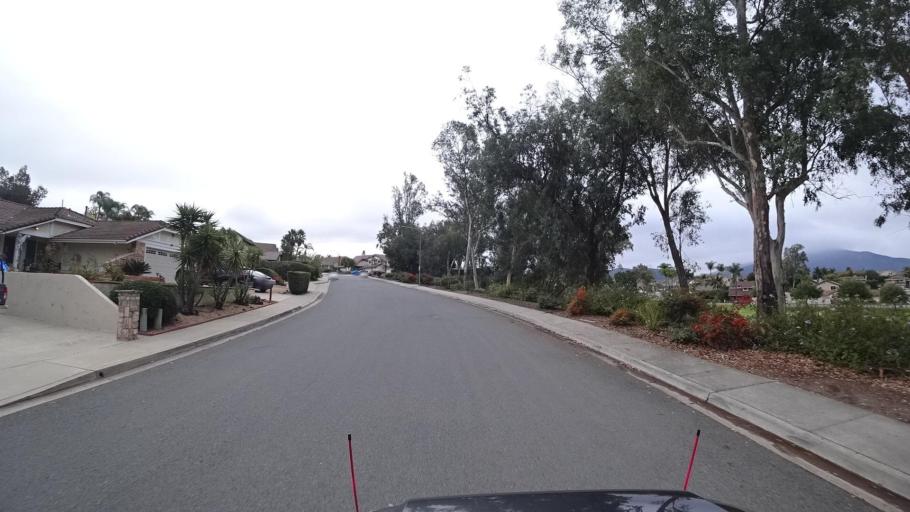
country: US
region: California
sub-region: San Diego County
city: Rancho San Diego
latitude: 32.7524
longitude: -116.9157
